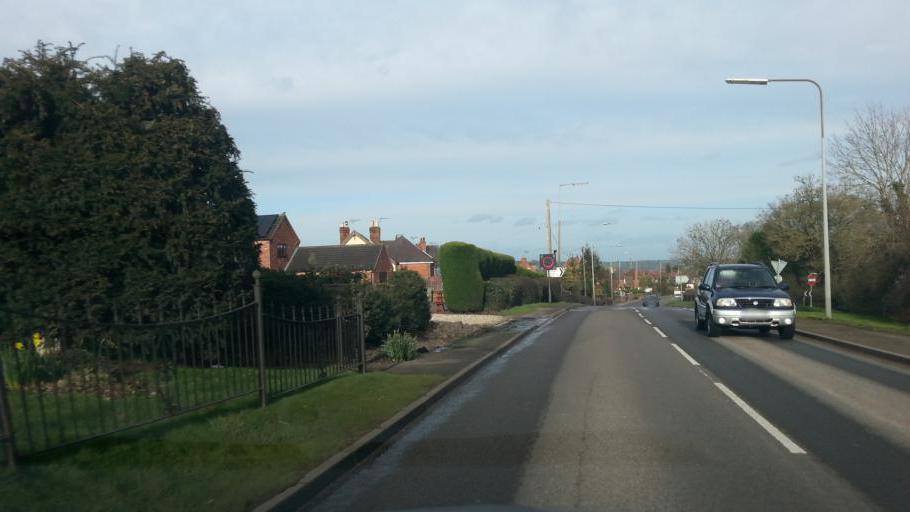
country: GB
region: England
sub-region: Staffordshire
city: Uttoxeter
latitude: 52.8899
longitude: -1.8836
